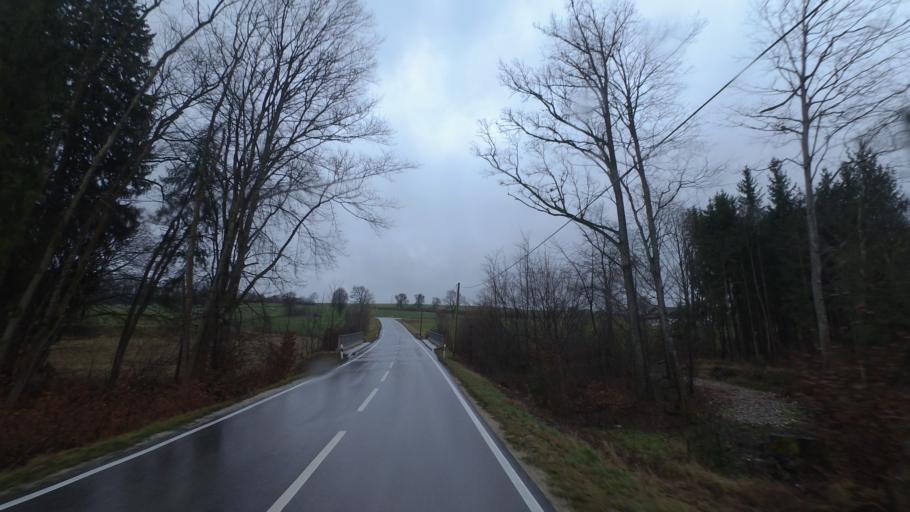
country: DE
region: Bavaria
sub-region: Upper Bavaria
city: Sankt Leonhard am Wonneberg
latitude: 47.9210
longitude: 12.7020
